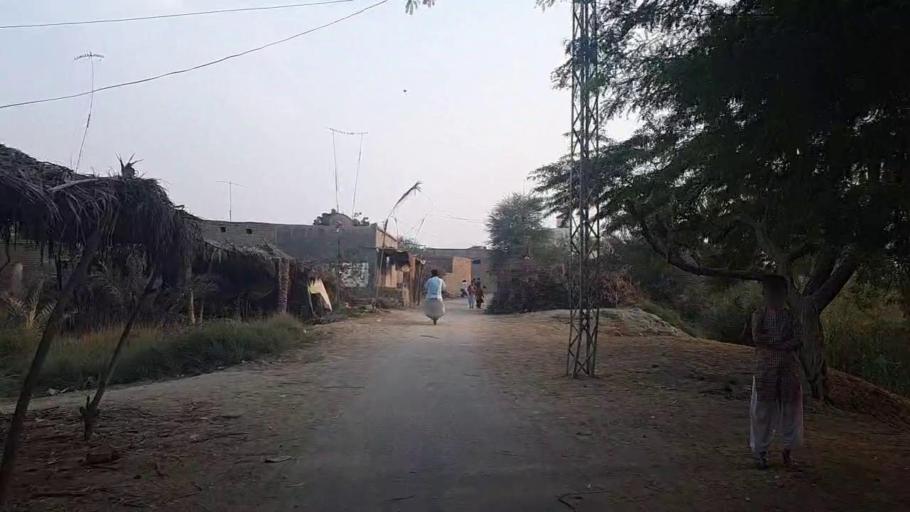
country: PK
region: Sindh
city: Kot Diji
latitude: 27.3775
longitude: 68.6657
